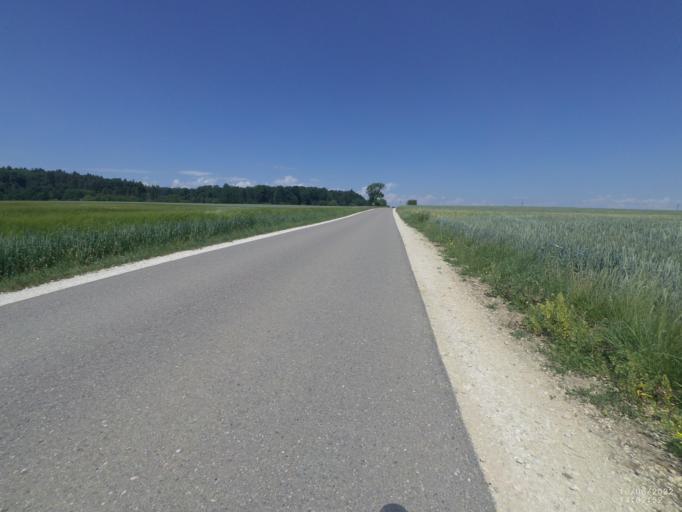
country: DE
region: Baden-Wuerttemberg
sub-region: Tuebingen Region
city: Ballendorf
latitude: 48.5894
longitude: 10.0685
